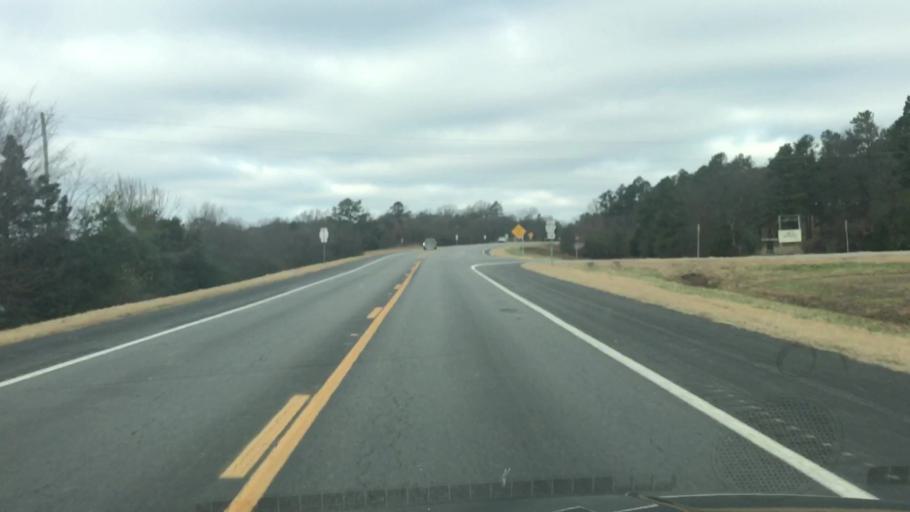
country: US
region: Arkansas
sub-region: Scott County
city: Waldron
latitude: 34.8816
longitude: -94.1029
